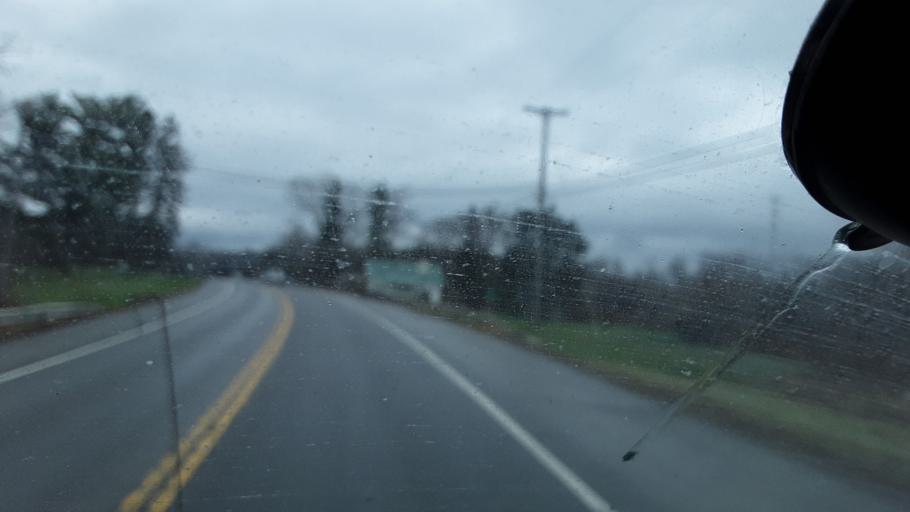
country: US
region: New York
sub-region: Cattaraugus County
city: Yorkshire
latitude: 42.5794
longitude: -78.4817
